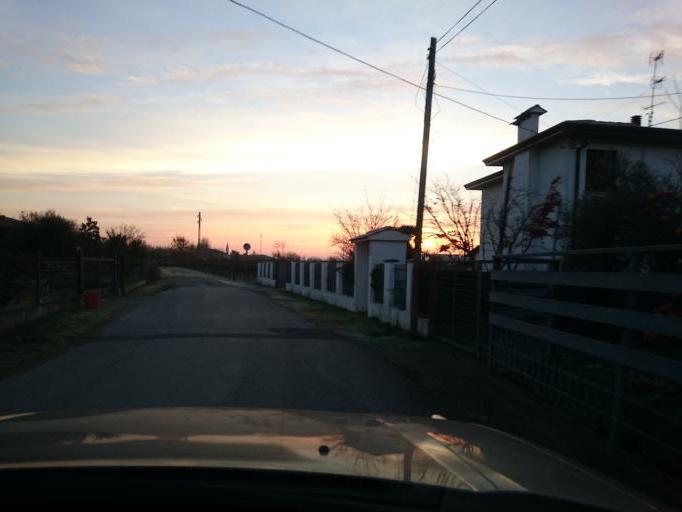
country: IT
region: Veneto
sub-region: Provincia di Padova
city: Carrara San Giorgio
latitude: 45.2942
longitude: 11.8037
